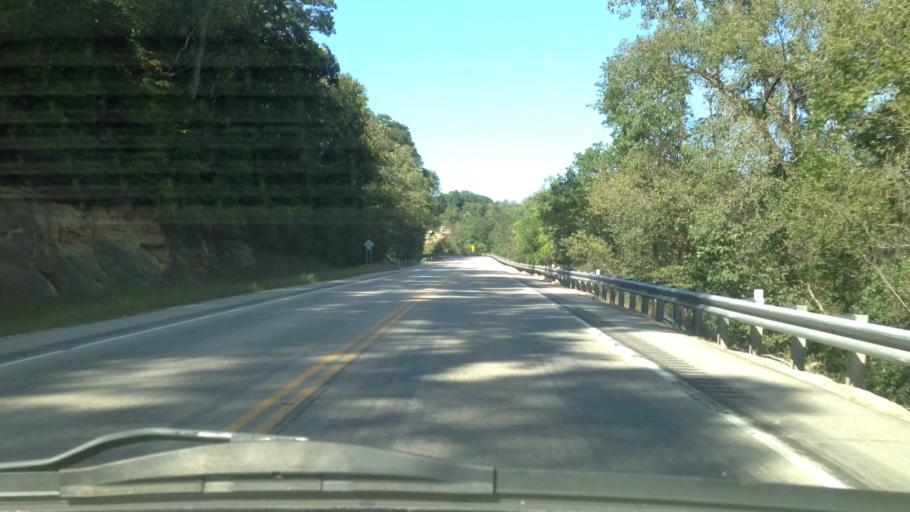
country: US
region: Minnesota
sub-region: Fillmore County
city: Rushford
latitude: 43.8408
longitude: -91.7544
